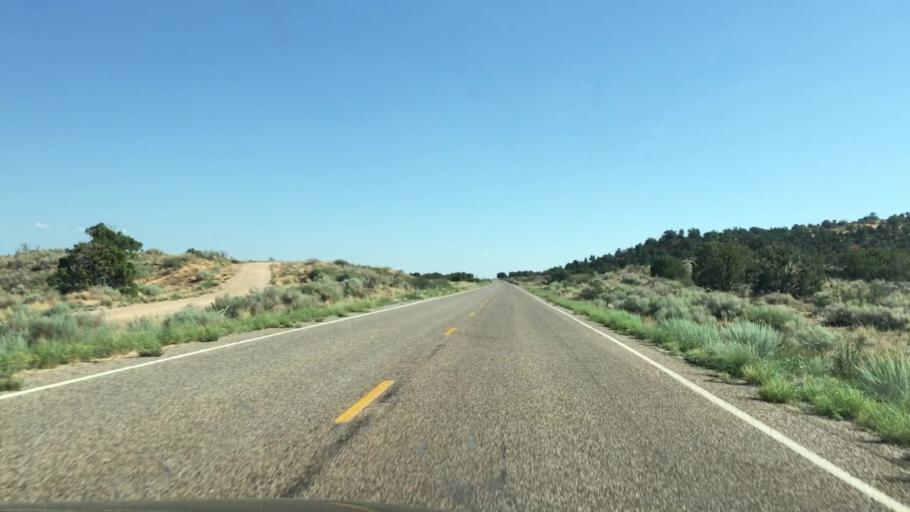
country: US
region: Arizona
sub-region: Coconino County
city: Fredonia
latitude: 36.8795
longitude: -112.7389
